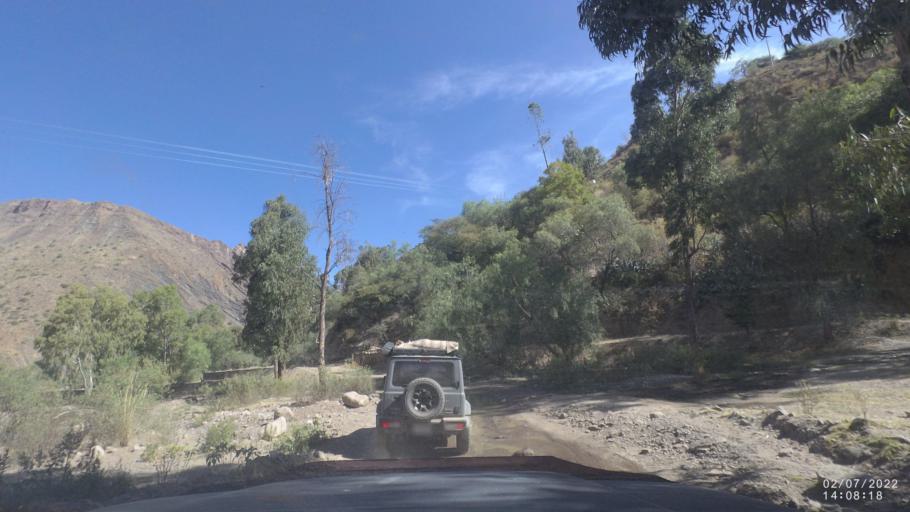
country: BO
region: Cochabamba
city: Irpa Irpa
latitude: -17.8191
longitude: -66.4020
